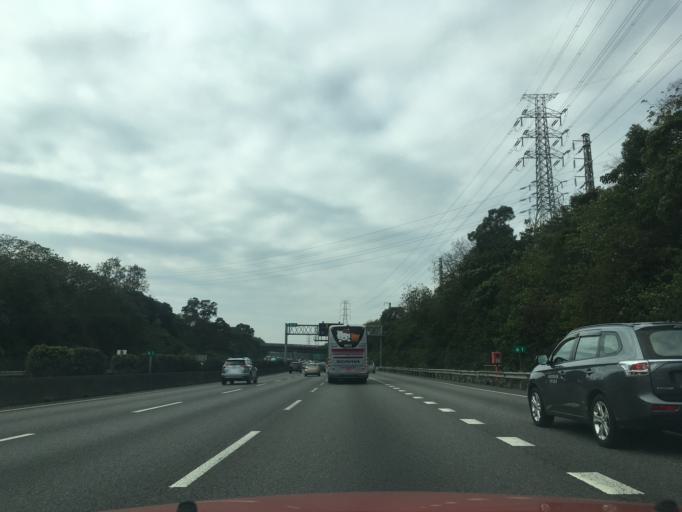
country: TW
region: Taiwan
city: Daxi
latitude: 24.9048
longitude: 121.2746
